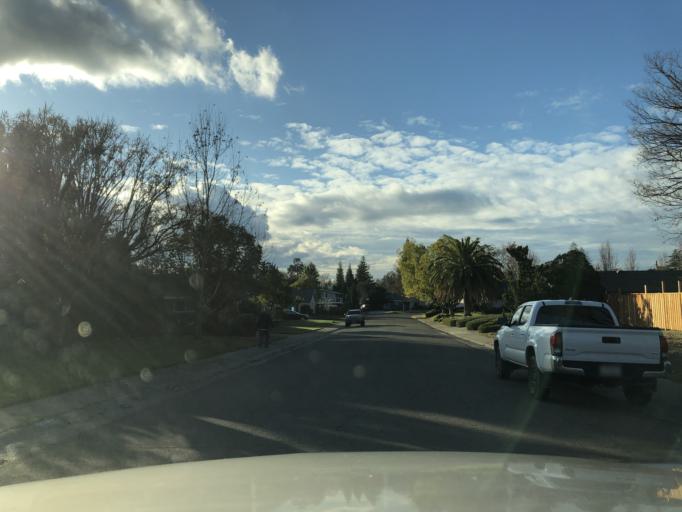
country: US
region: California
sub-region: Sacramento County
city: Fair Oaks
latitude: 38.6622
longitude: -121.3087
